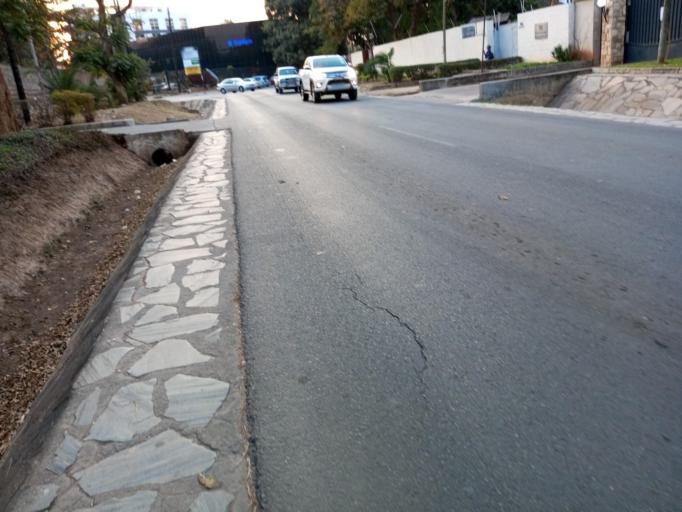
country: ZM
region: Lusaka
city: Lusaka
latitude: -15.4087
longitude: 28.3013
